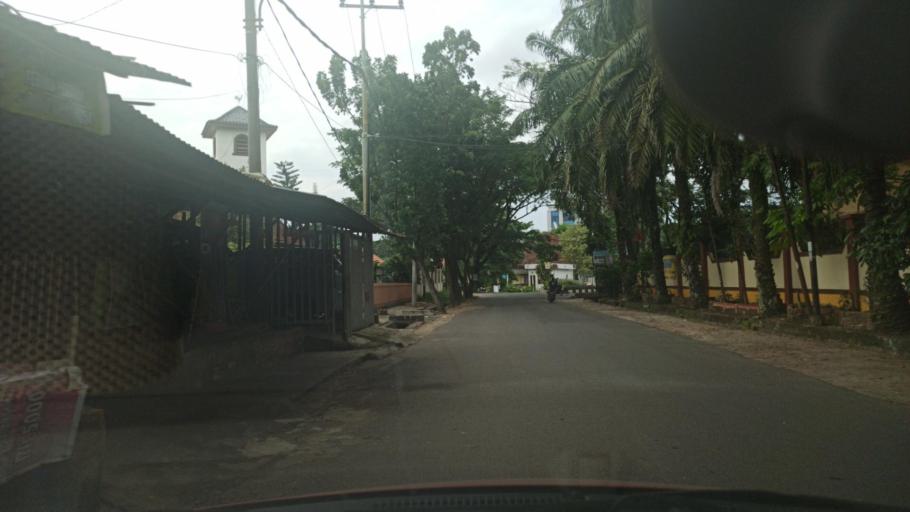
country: ID
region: South Sumatra
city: Plaju
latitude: -2.9925
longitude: 104.7529
